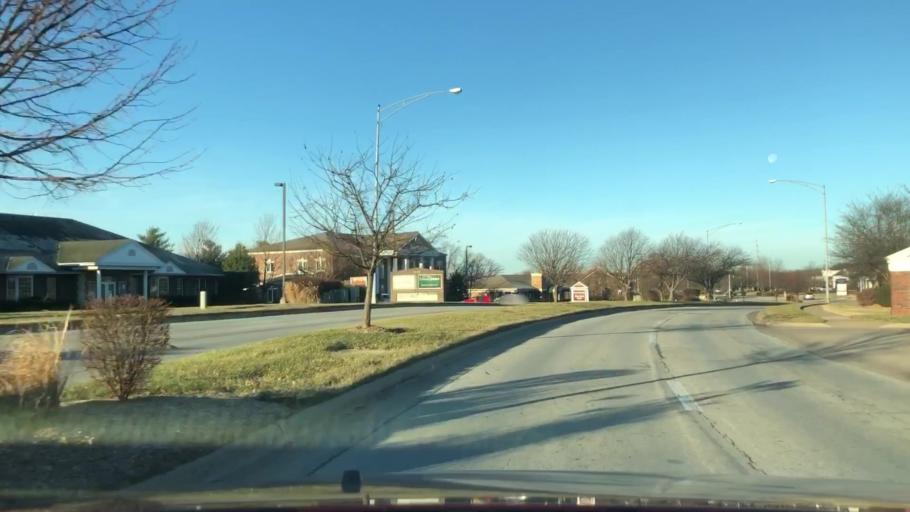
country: US
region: Missouri
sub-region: Greene County
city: Springfield
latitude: 37.1471
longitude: -93.2682
